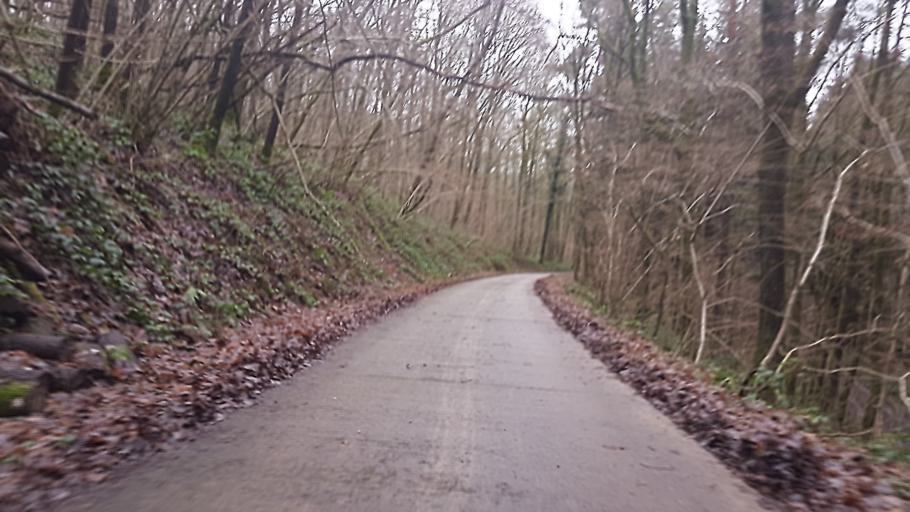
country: BE
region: Wallonia
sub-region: Province de Namur
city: Couvin
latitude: 50.0587
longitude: 4.5984
